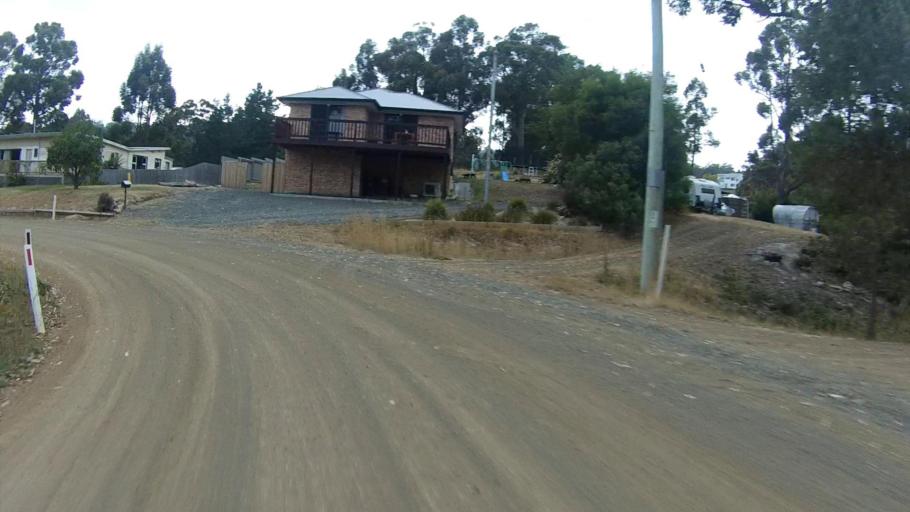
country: AU
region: Tasmania
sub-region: Huon Valley
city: Cygnet
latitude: -43.2290
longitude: 147.0991
